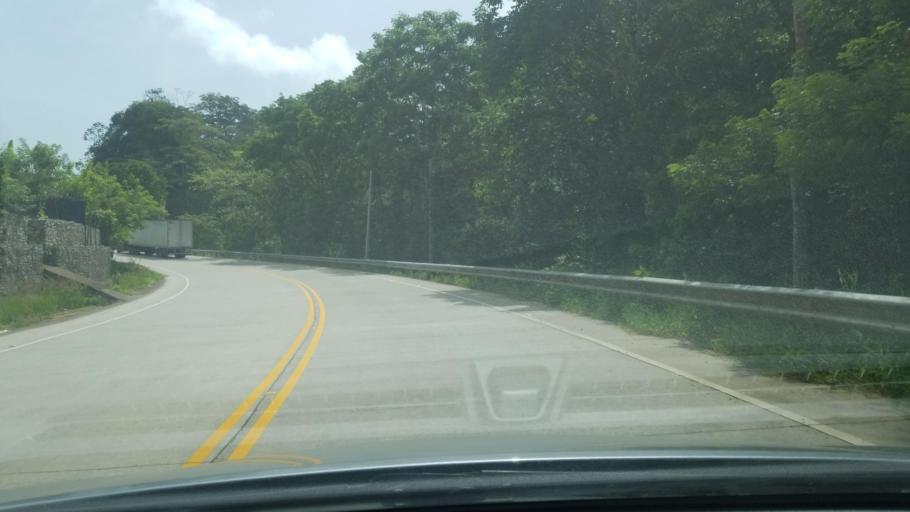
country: HN
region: Copan
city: San Jeronimo
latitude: 14.9471
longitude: -88.9109
